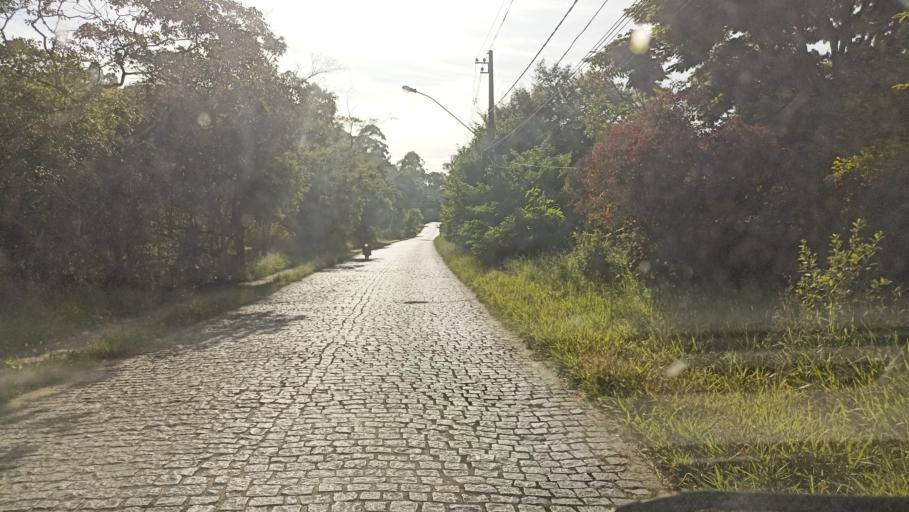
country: BR
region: Minas Gerais
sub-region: Tiradentes
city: Tiradentes
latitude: -21.1196
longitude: -44.2011
